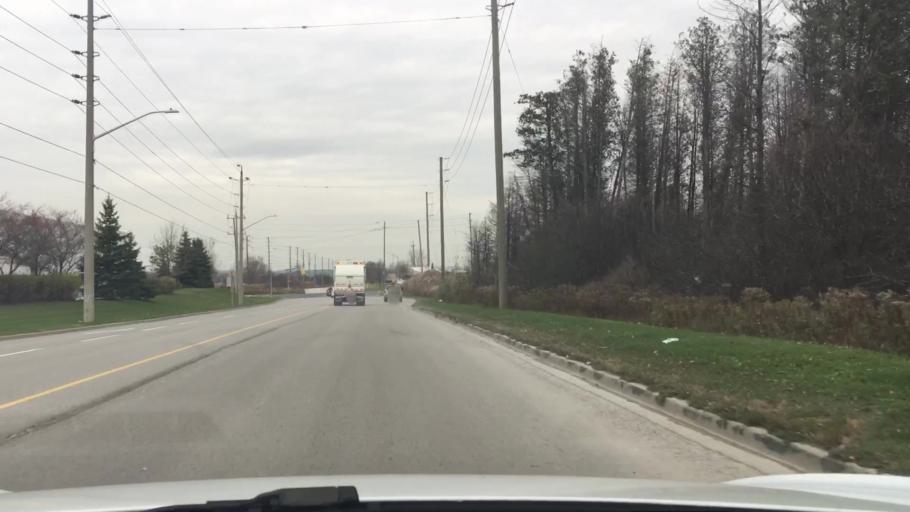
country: CA
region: Ontario
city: Ajax
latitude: 43.8335
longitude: -79.0568
